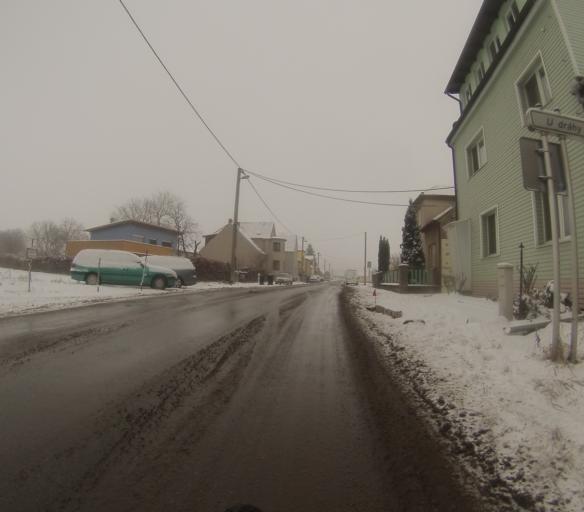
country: CZ
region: South Moravian
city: Troubsko
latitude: 49.1636
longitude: 16.5264
